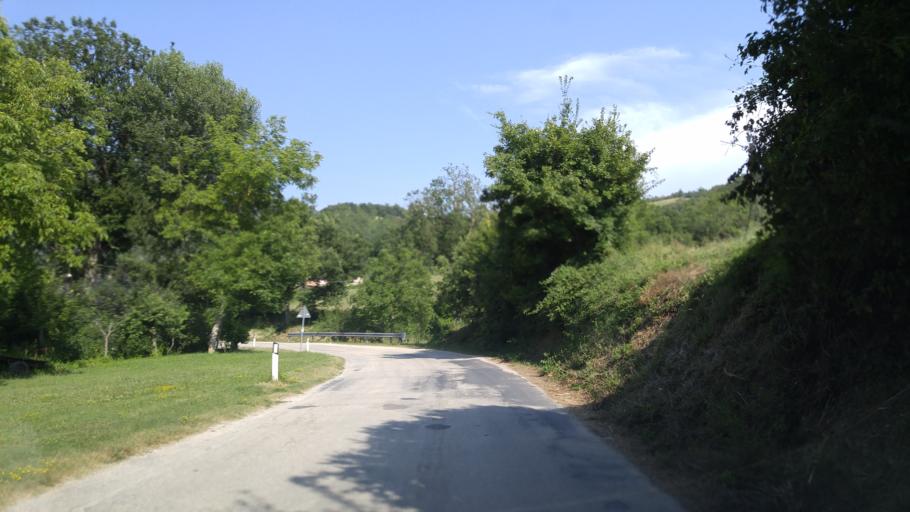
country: IT
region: The Marches
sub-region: Provincia di Pesaro e Urbino
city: Acqualagna
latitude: 43.6337
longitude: 12.7008
